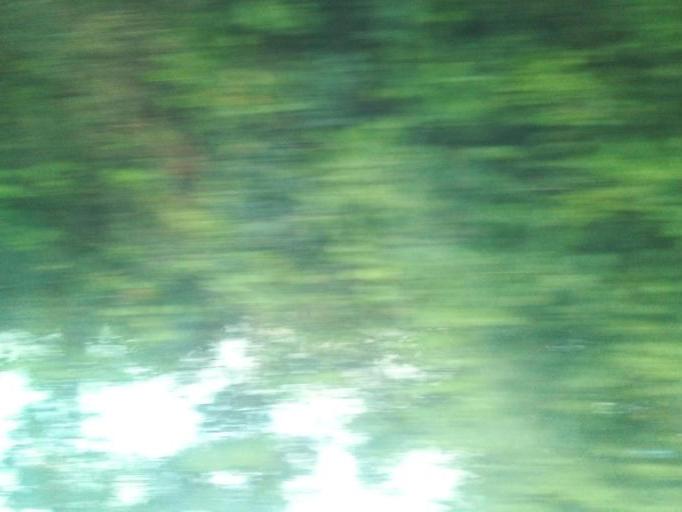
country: BR
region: Maranhao
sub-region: Imperatriz
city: Imperatriz
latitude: -4.9272
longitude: -47.4260
